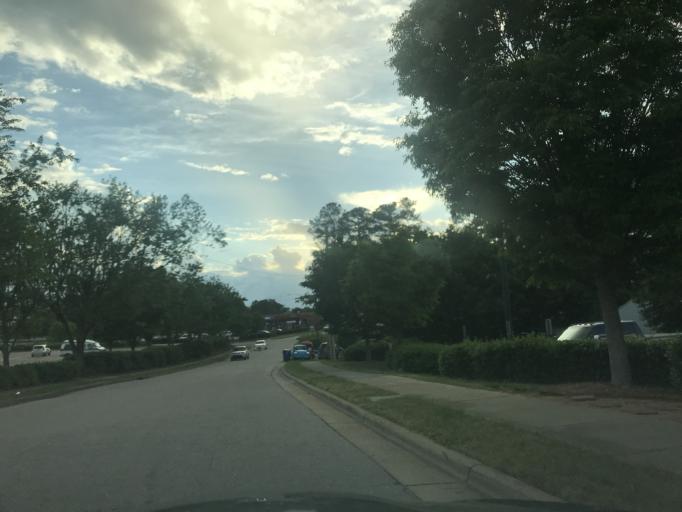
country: US
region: North Carolina
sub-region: Wake County
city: Raleigh
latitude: 35.8382
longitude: -78.6083
